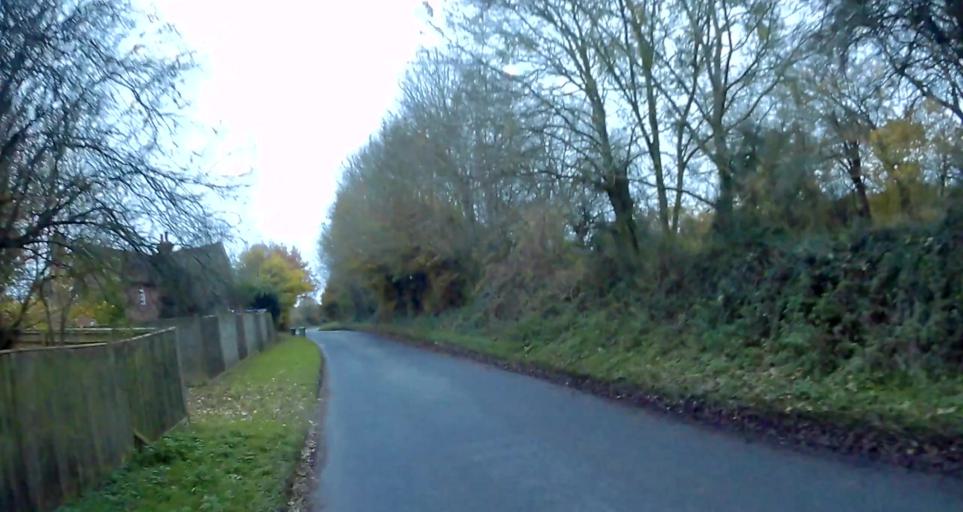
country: GB
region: England
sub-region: Hampshire
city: Odiham
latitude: 51.2381
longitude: -0.9860
